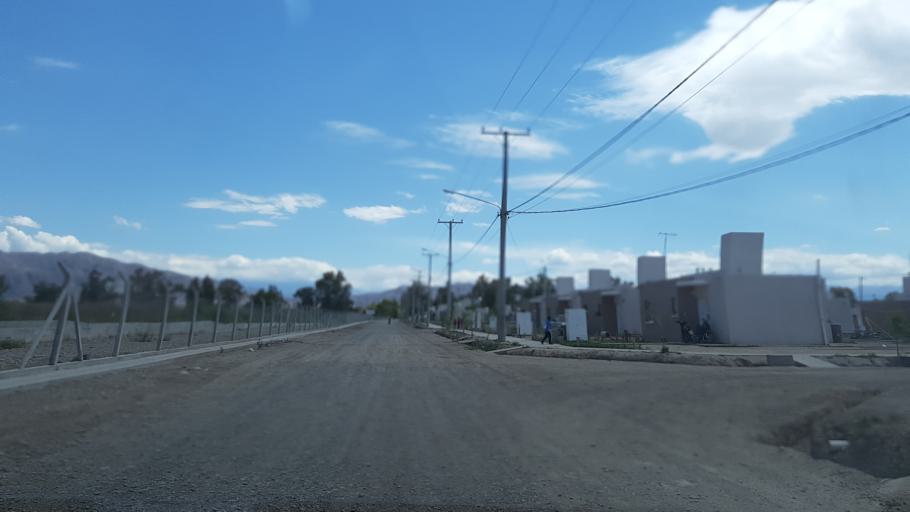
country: AR
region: San Juan
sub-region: Departamento de Rivadavia
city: Rivadavia
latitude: -31.5568
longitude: -68.6058
